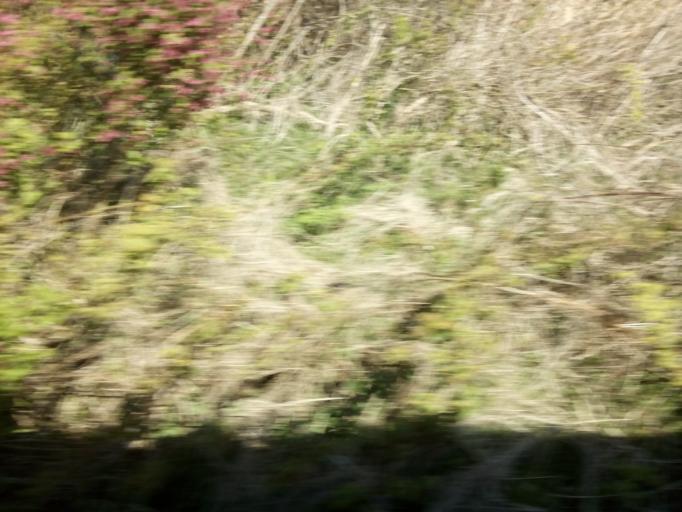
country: GB
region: Scotland
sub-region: Fife
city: Kirkcaldy
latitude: 56.1242
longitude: -3.1337
